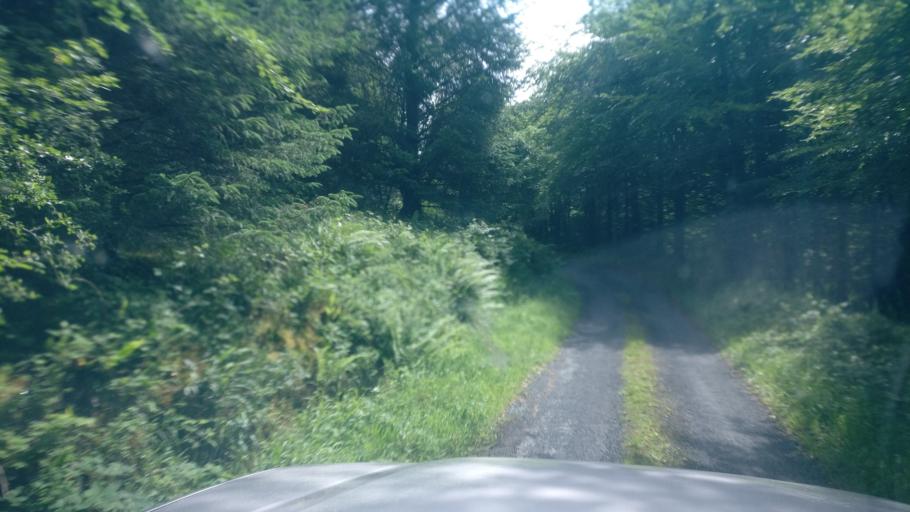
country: IE
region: Connaught
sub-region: County Galway
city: Gort
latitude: 53.0629
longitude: -8.6982
